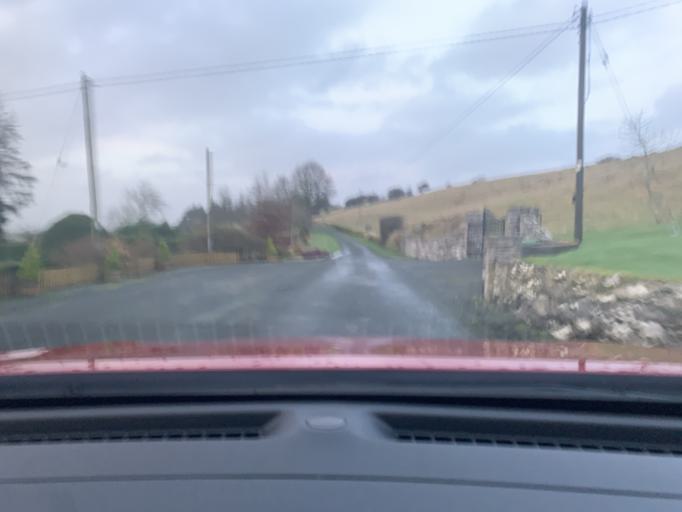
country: IE
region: Connaught
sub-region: Sligo
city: Ballymote
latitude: 54.0547
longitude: -8.3963
